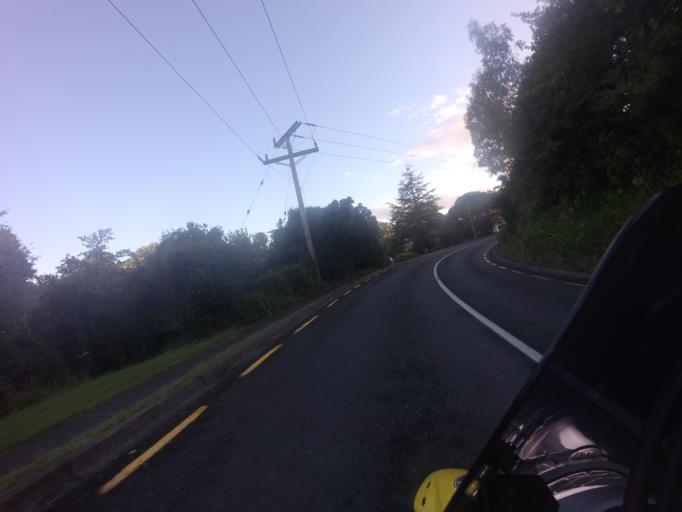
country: NZ
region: Gisborne
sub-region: Gisborne District
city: Gisborne
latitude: -38.6659
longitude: 178.0514
